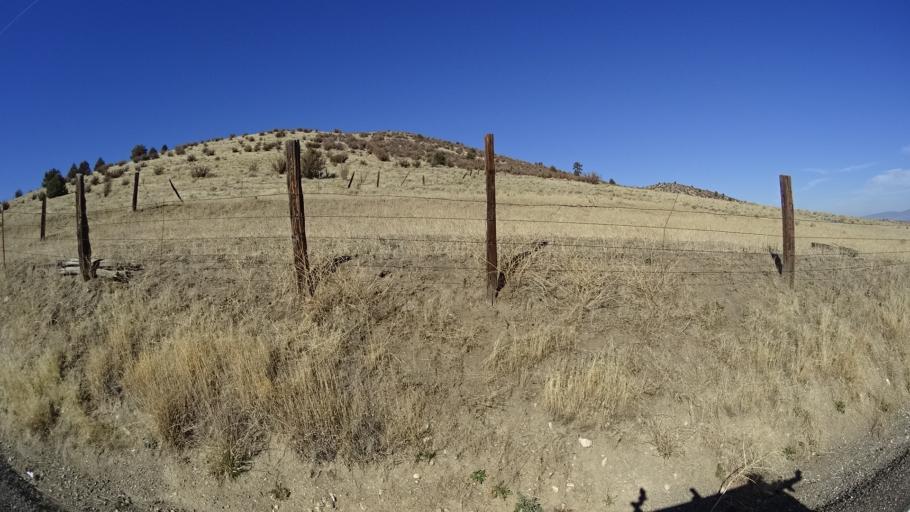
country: US
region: California
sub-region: Siskiyou County
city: Weed
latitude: 41.5084
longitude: -122.5327
